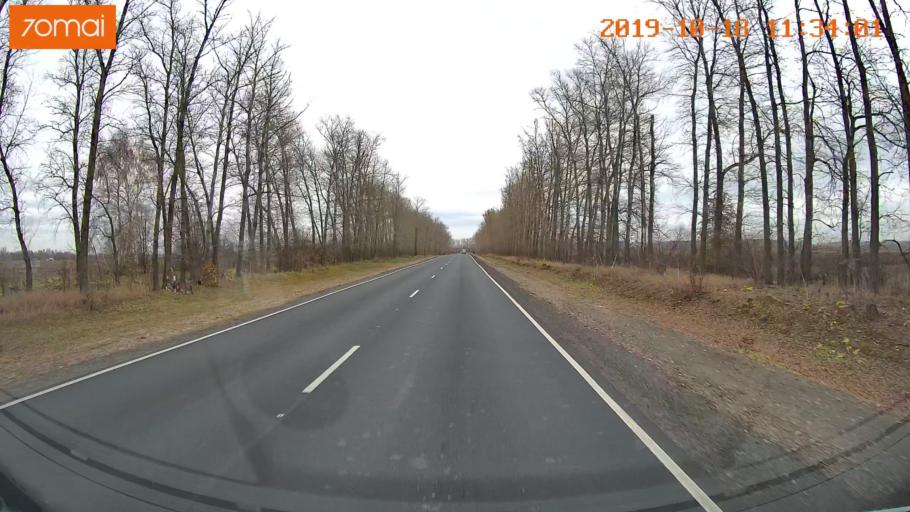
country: RU
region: Rjazan
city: Oktyabr'skiy
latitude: 54.1375
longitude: 38.7548
